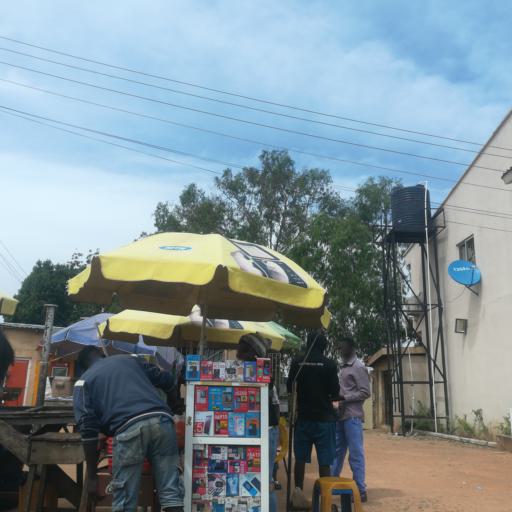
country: NG
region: Plateau
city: Jos
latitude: 9.8773
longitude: 8.8735
